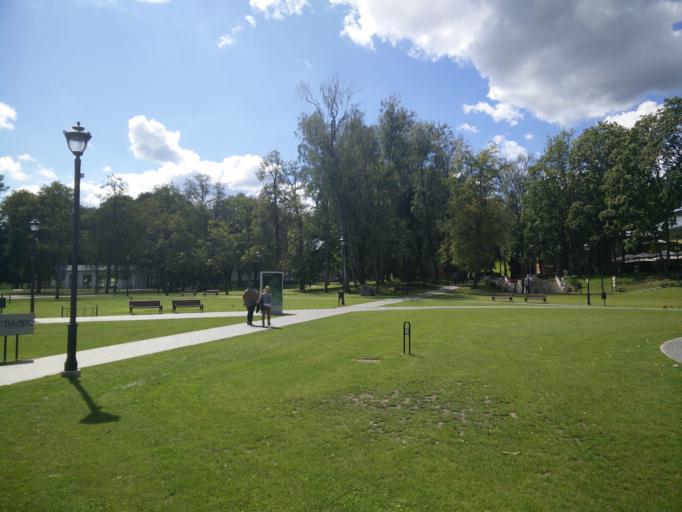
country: LT
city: Birstonas
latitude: 54.6009
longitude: 24.0348
